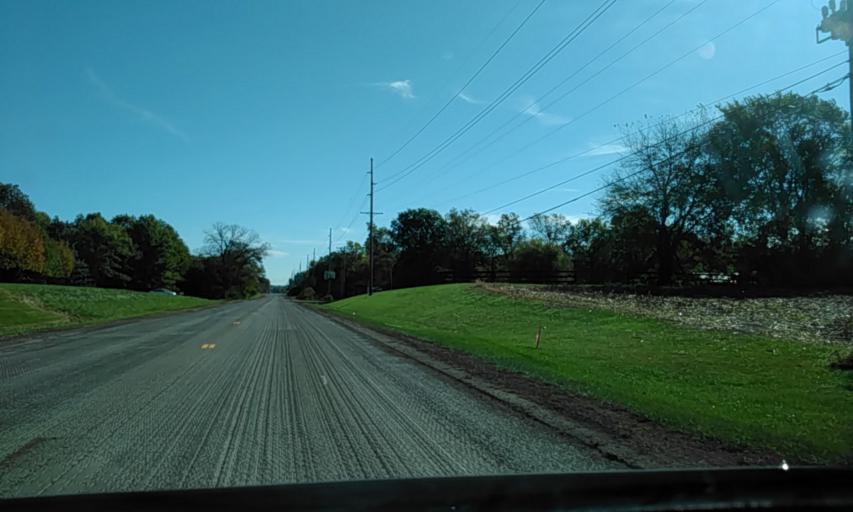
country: US
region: Illinois
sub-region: Madison County
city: Troy
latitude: 38.7177
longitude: -89.8641
